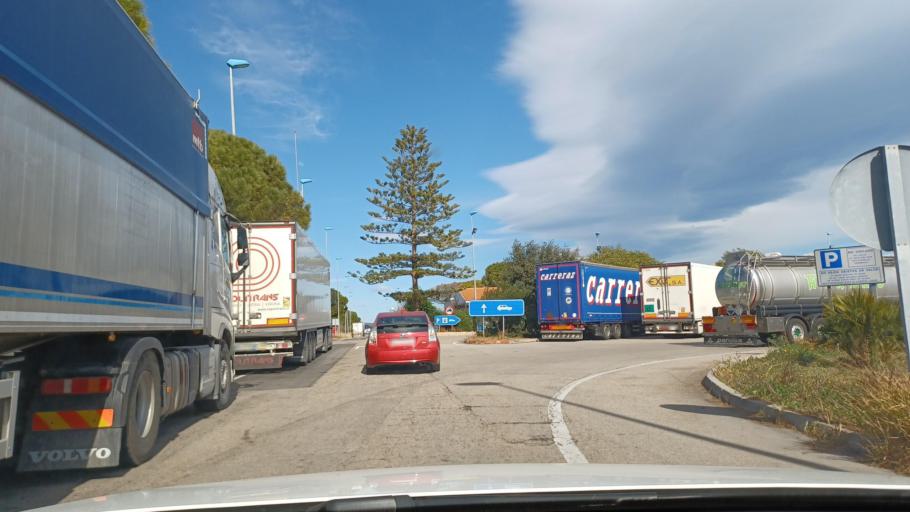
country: ES
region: Valencia
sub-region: Provincia de Castello
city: Orpesa/Oropesa del Mar
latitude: 40.1321
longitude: 0.1400
